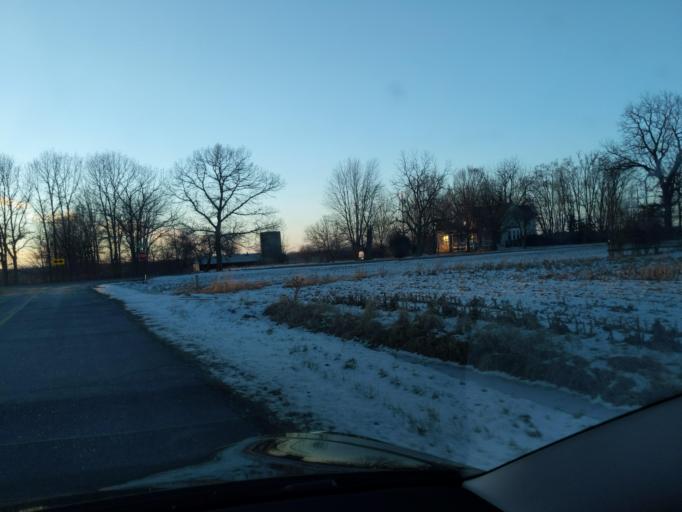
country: US
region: Michigan
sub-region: Ingham County
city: Stockbridge
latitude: 42.4536
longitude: -84.2771
